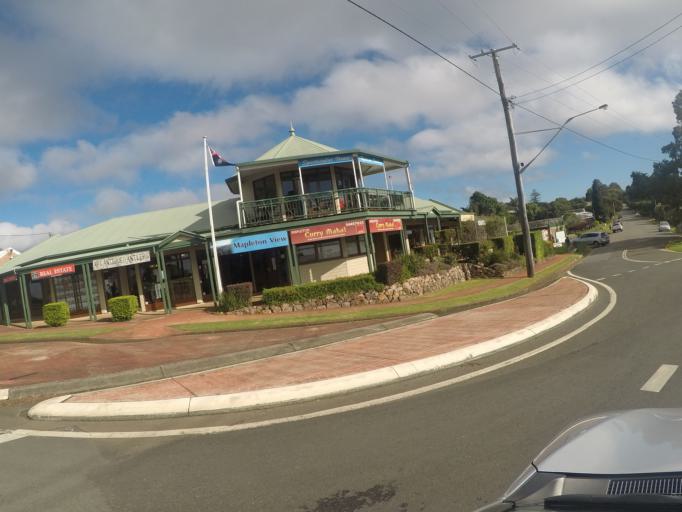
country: AU
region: Queensland
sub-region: Sunshine Coast
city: Nambour
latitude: -26.6239
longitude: 152.8663
